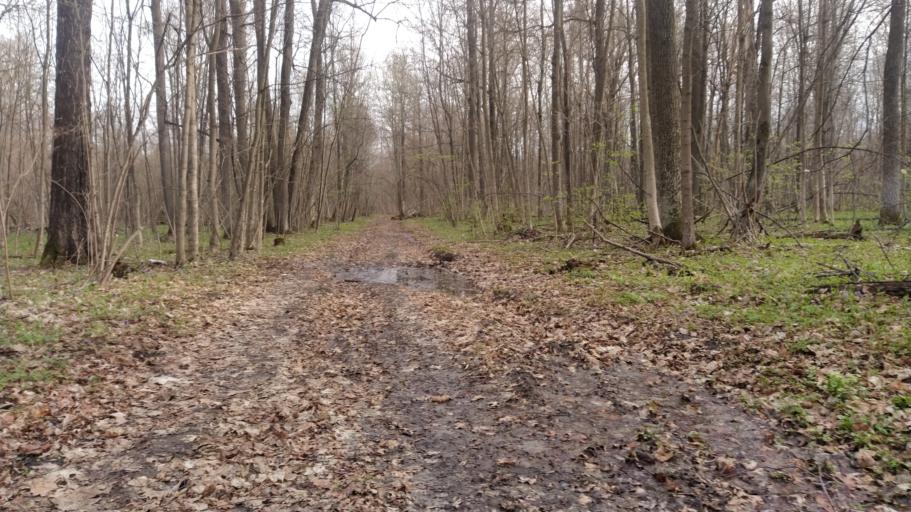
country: RU
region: Chuvashia
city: Novyye Lapsary
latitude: 56.1344
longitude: 47.1211
